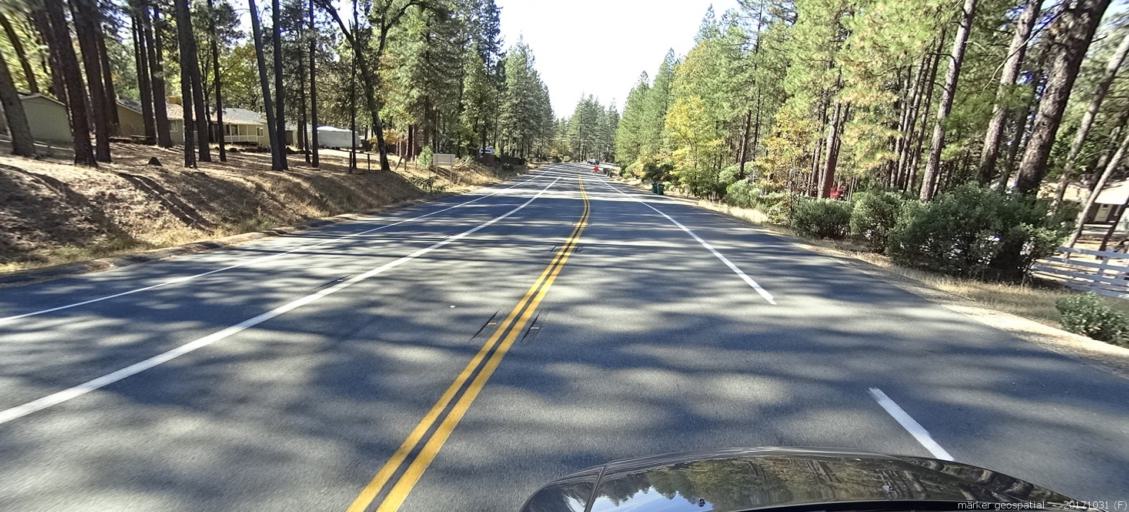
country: US
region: California
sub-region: Shasta County
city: Shingletown
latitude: 40.5099
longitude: -121.9394
